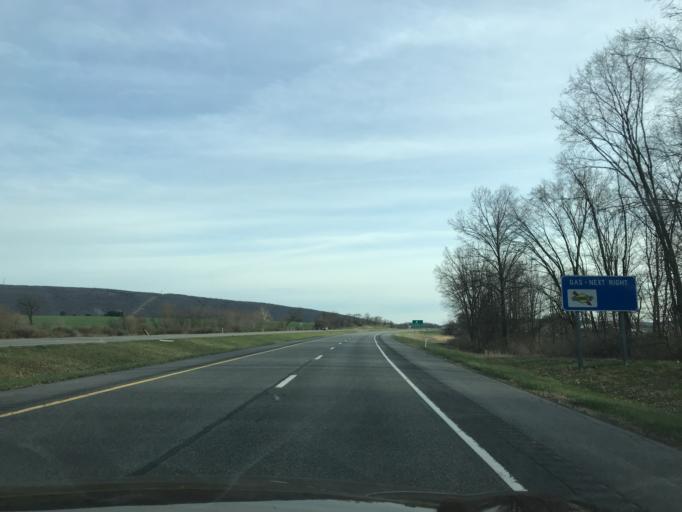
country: US
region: Pennsylvania
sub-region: Northumberland County
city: Milton
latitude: 40.9740
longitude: -76.8400
